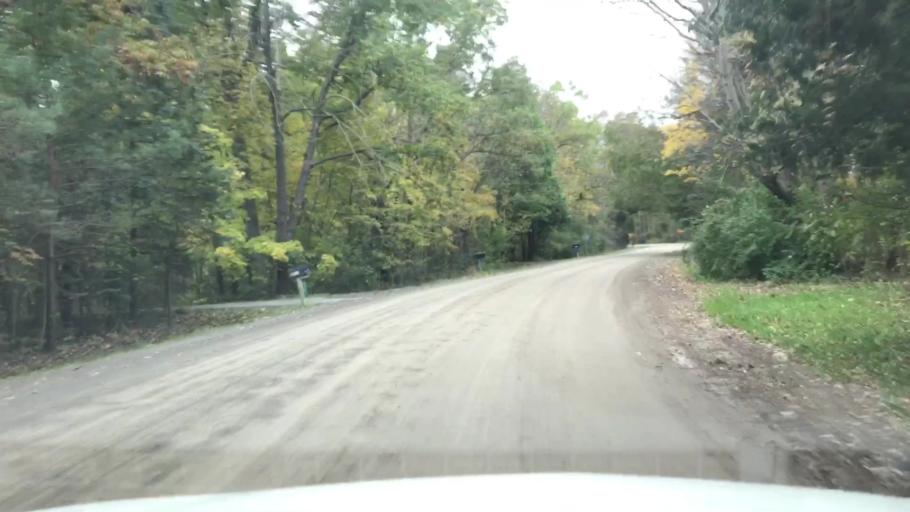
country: US
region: Michigan
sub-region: Oakland County
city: Rochester
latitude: 42.7454
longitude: -83.0991
